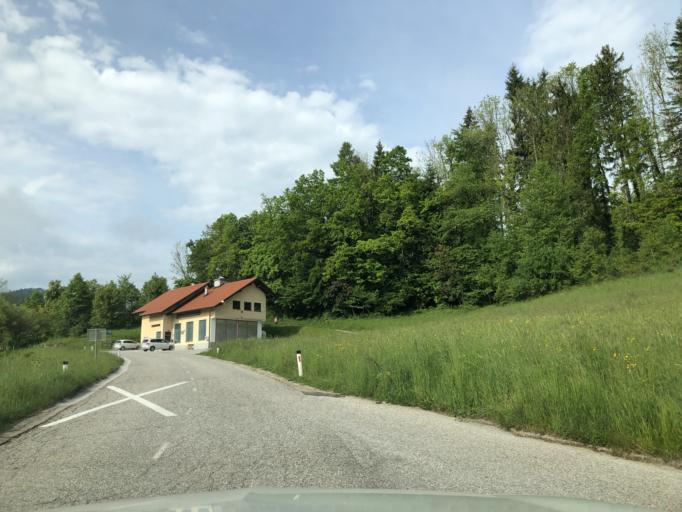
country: SI
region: Velike Lasce
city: Velike Lasce
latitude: 45.8082
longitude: 14.6050
